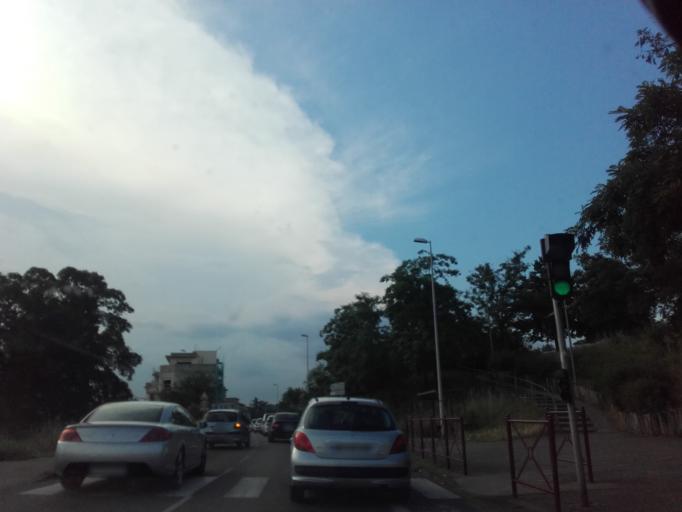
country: FR
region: Rhone-Alpes
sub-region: Departement de l'Isere
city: Le Peage-de-Roussillon
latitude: 45.3746
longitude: 4.8004
